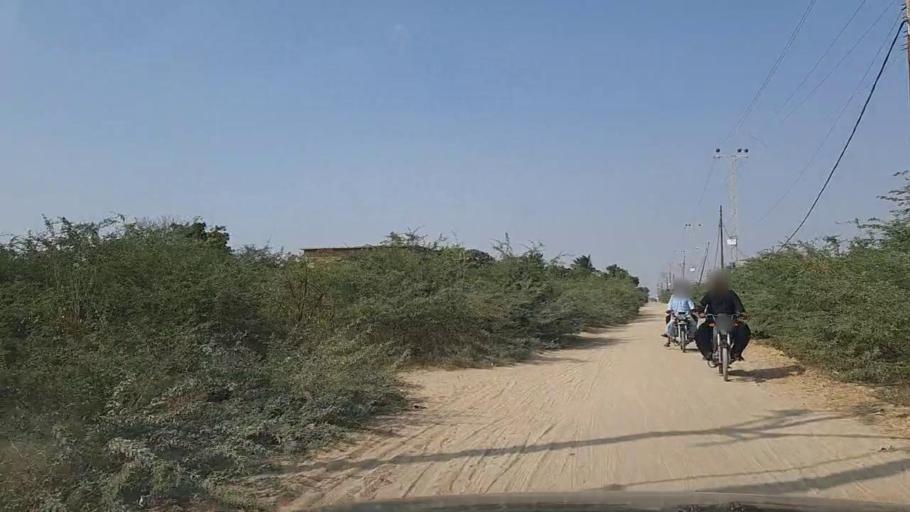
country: PK
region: Sindh
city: Gharo
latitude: 24.7499
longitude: 67.5817
